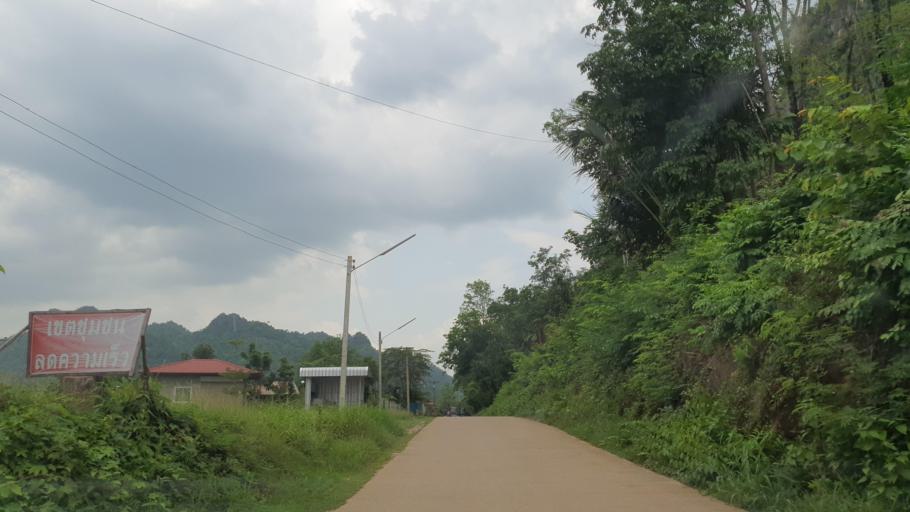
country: TH
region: Sukhothai
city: Thung Saliam
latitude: 17.3173
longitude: 99.5106
